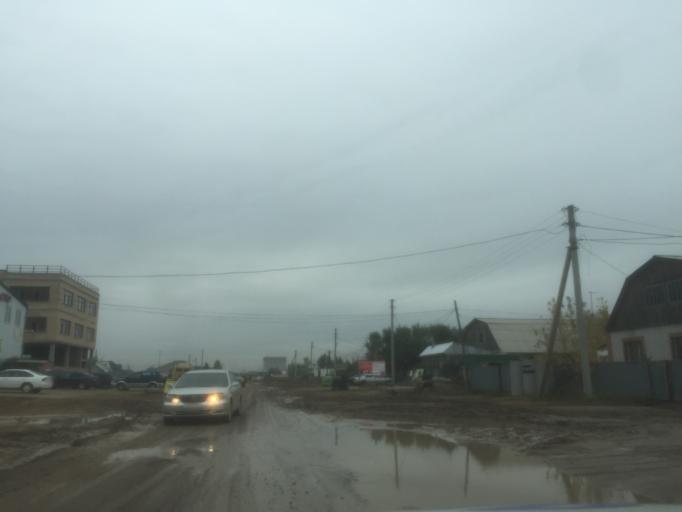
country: KZ
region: Astana Qalasy
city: Astana
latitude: 51.1912
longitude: 71.3416
